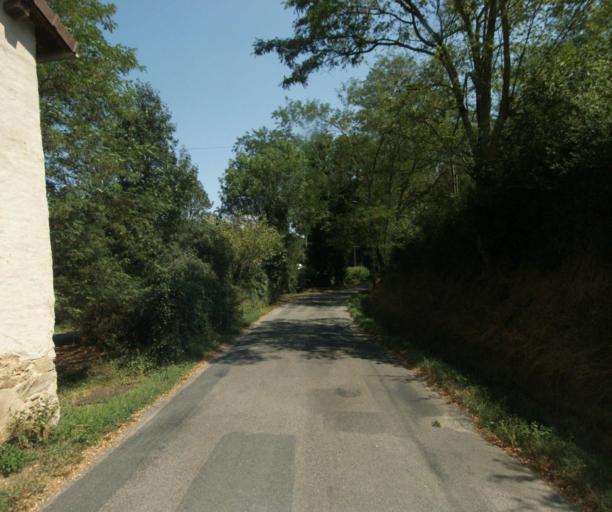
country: FR
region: Rhone-Alpes
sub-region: Departement du Rhone
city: Sourcieux-les-Mines
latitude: 45.7990
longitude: 4.6344
